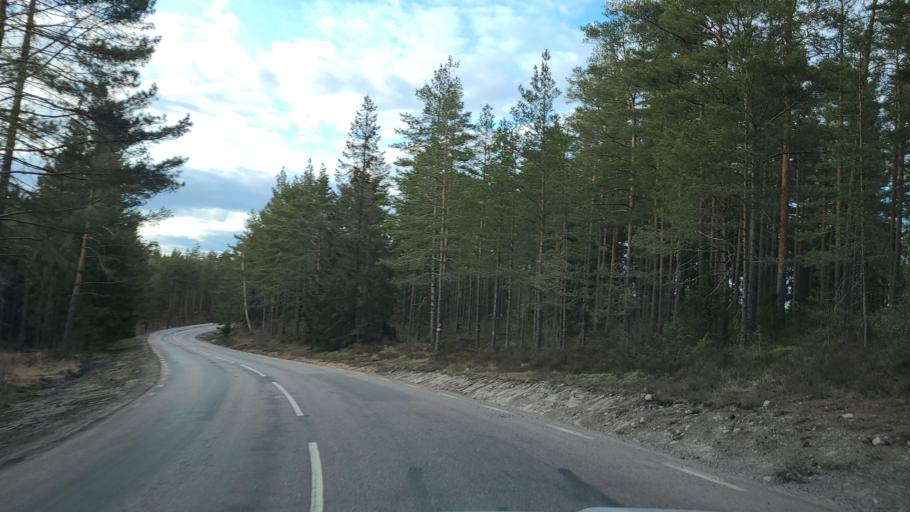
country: SE
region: Soedermanland
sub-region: Nykopings Kommun
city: Olstorp
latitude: 58.7165
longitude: 16.6572
